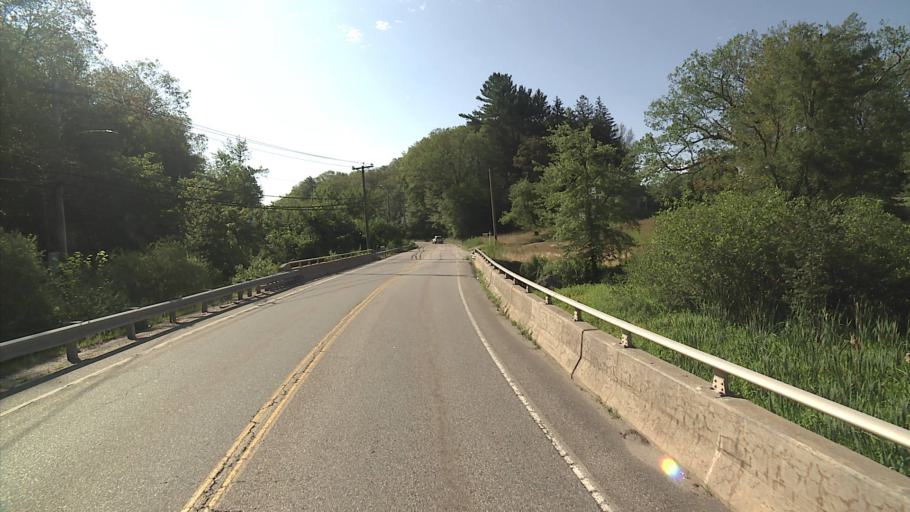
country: US
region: Connecticut
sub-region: New London County
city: Uncasville
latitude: 41.4380
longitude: -72.1127
